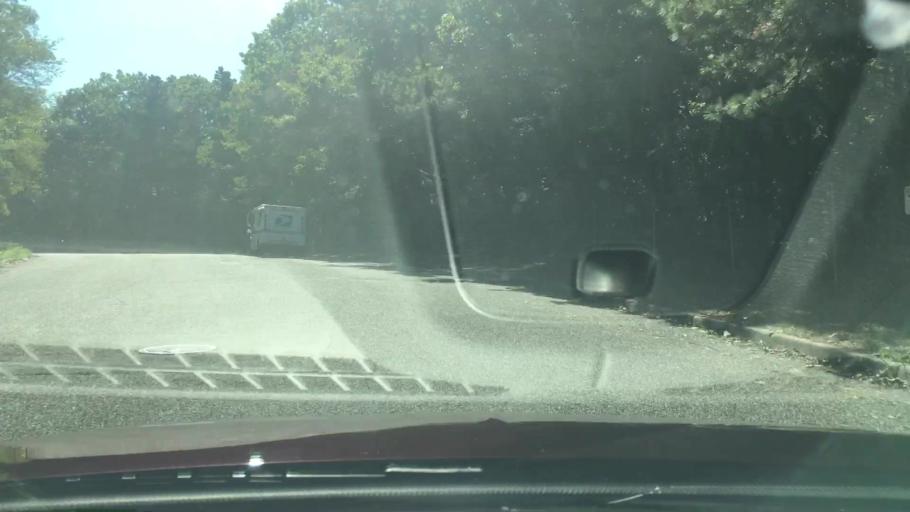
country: US
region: New York
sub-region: Suffolk County
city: Yaphank
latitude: 40.8431
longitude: -72.8853
